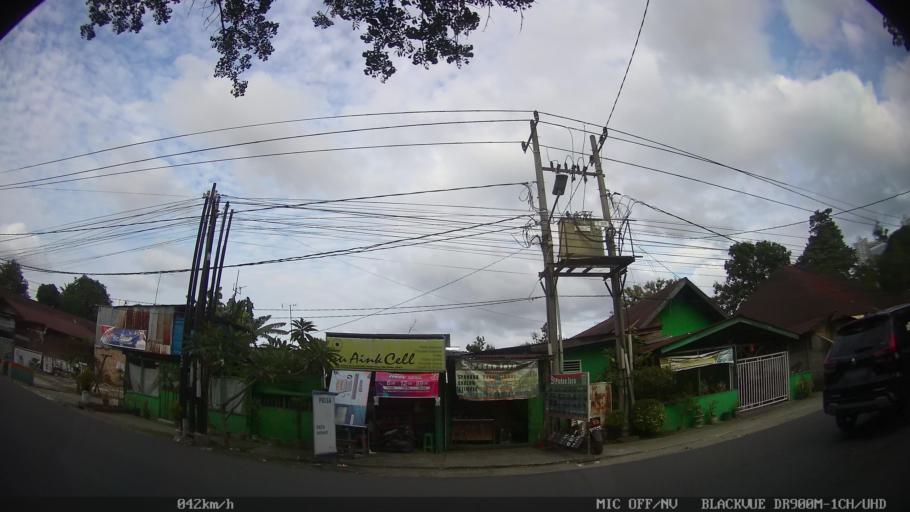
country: ID
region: North Sumatra
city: Medan
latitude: 3.6005
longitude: 98.6771
